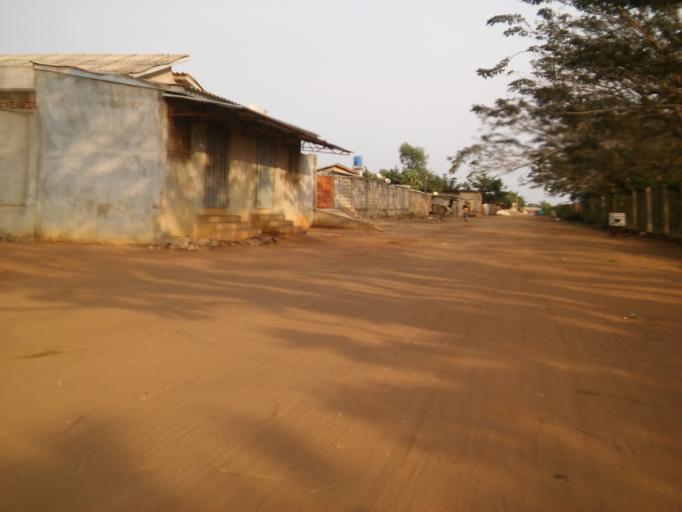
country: BJ
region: Atlantique
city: Abomey-Calavi
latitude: 6.4202
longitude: 2.3324
